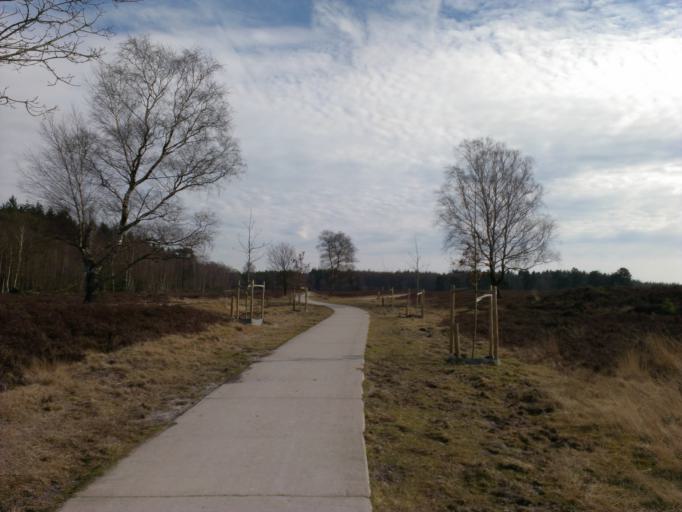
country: NL
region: Gelderland
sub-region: Gemeente Epe
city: Epe
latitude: 52.3888
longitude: 5.9867
